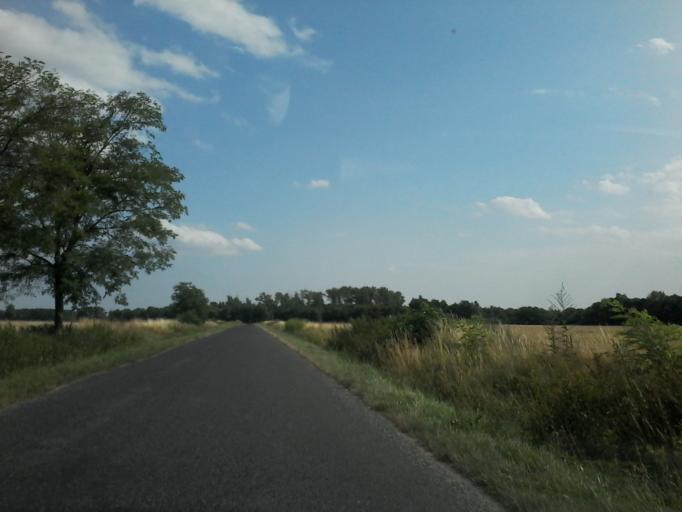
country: HU
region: Vas
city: Celldomolk
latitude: 47.2105
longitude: 17.0929
